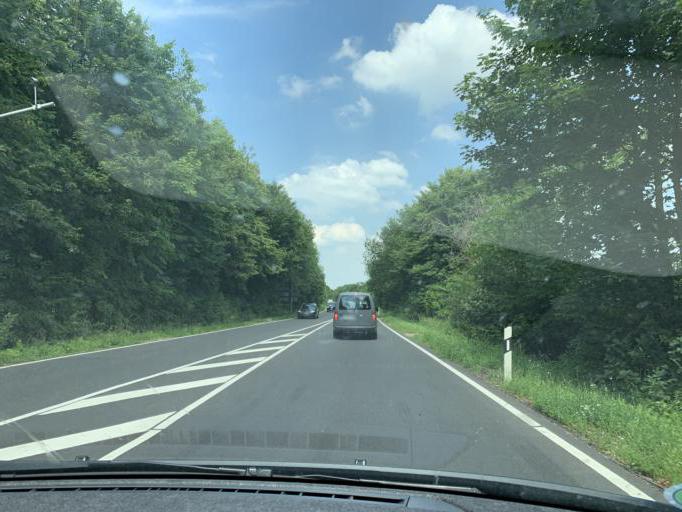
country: DE
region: North Rhine-Westphalia
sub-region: Regierungsbezirk Koln
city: Eschweiler
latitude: 50.8380
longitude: 6.2459
